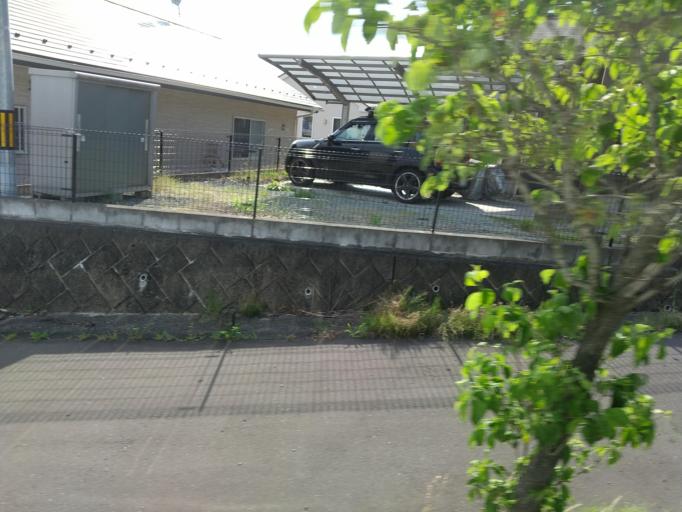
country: JP
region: Miyagi
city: Sendai
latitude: 38.2280
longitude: 140.7272
